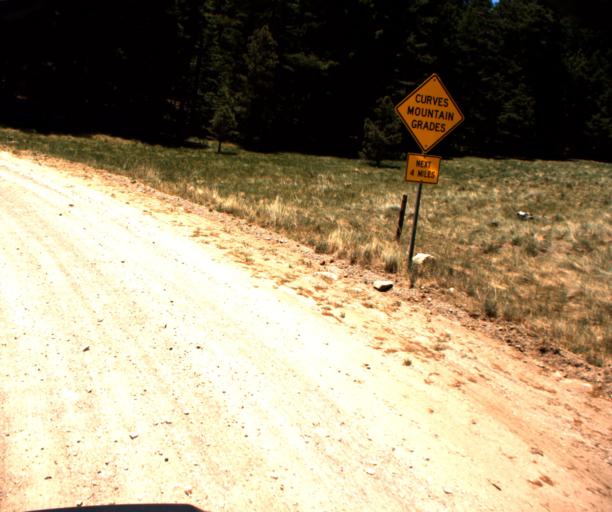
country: US
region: Arizona
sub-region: Graham County
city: Swift Trail Junction
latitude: 32.6702
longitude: -109.8782
